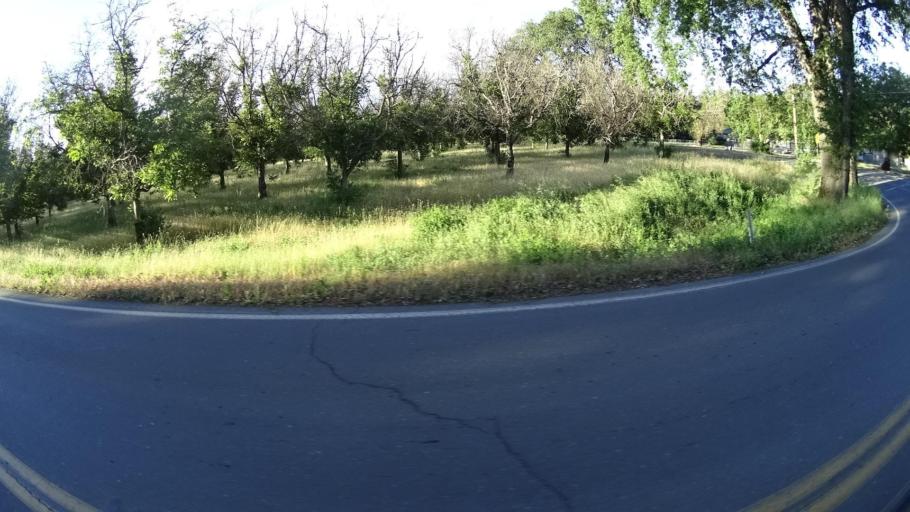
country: US
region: California
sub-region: Lake County
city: Upper Lake
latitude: 39.1718
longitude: -122.9113
